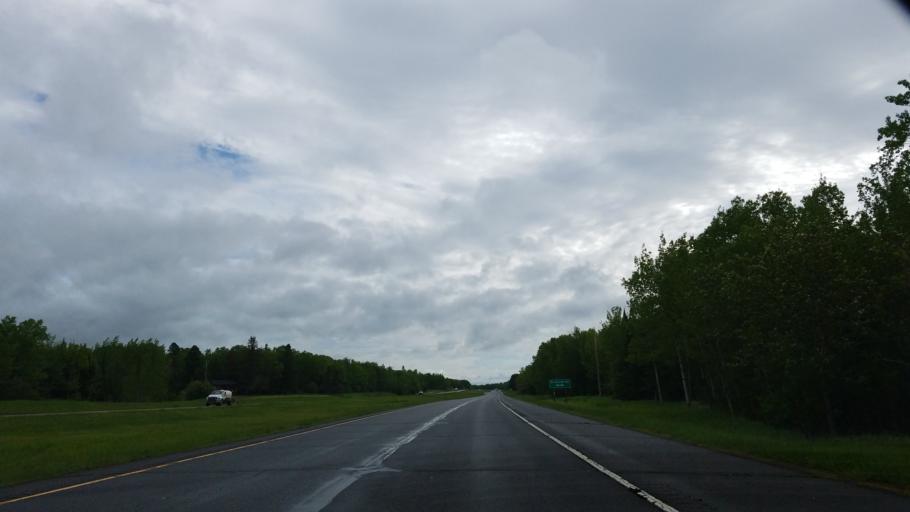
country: US
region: Minnesota
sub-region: Saint Louis County
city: Arnold
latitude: 46.8860
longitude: -91.9279
